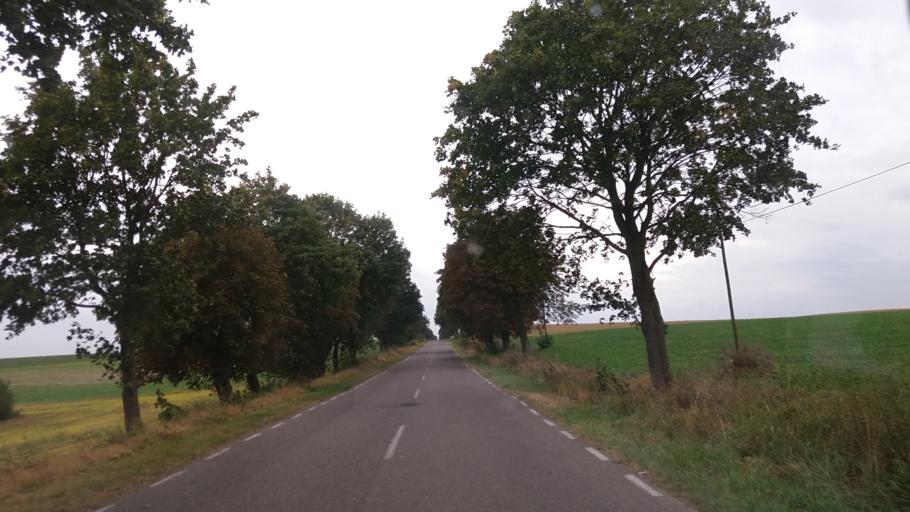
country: PL
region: Lubusz
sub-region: Powiat strzelecko-drezdenecki
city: Strzelce Krajenskie
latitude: 52.9629
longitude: 15.5798
